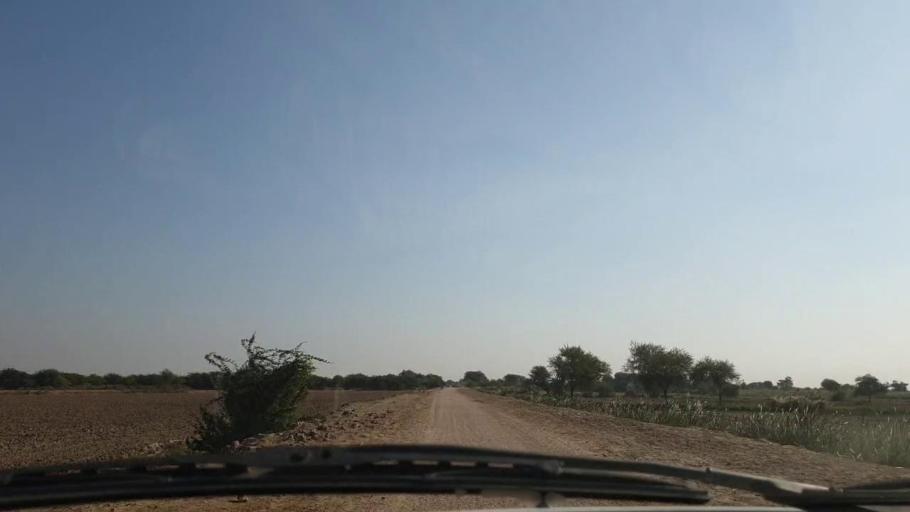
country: PK
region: Sindh
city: Bulri
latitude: 24.7977
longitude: 68.3944
